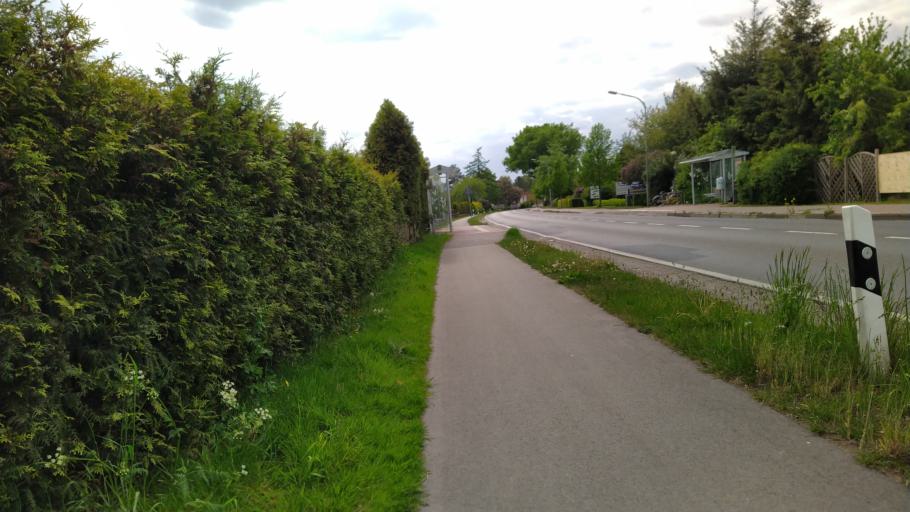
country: DE
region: Lower Saxony
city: Tarmstedt
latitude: 53.2268
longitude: 9.0912
